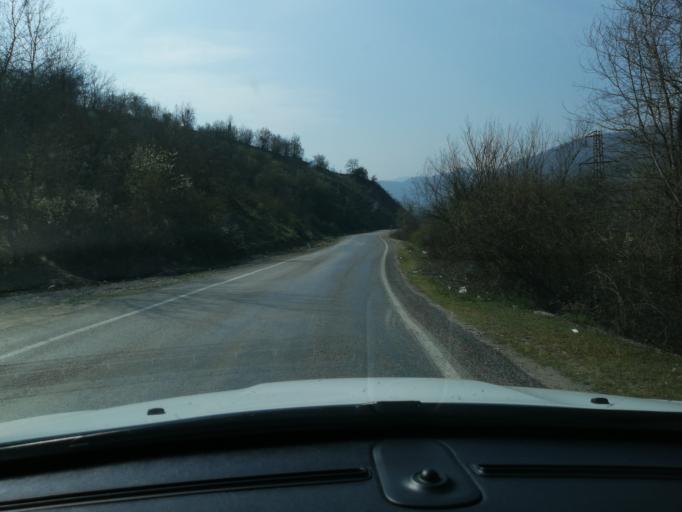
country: TR
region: Karabuk
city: Yenice
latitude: 41.2339
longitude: 32.3606
